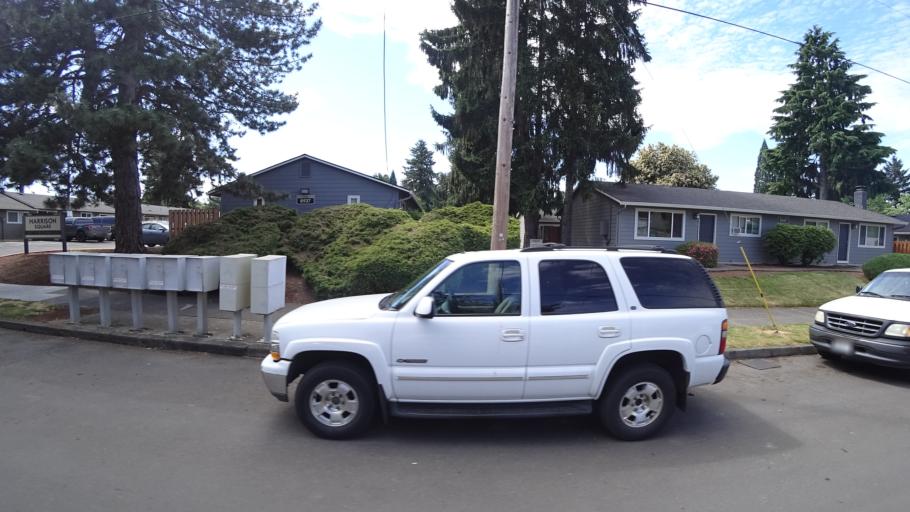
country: US
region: Oregon
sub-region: Washington County
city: West Haven
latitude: 45.5874
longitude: -122.7313
